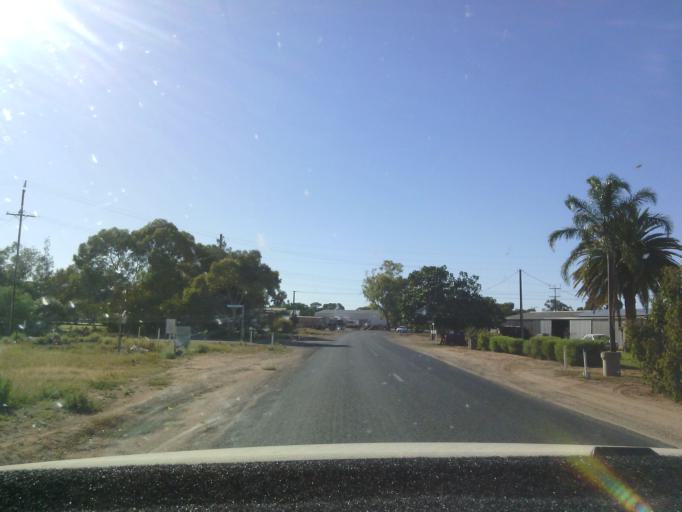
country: AU
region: South Australia
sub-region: Berri and Barmera
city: Berri
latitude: -34.2670
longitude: 140.6019
